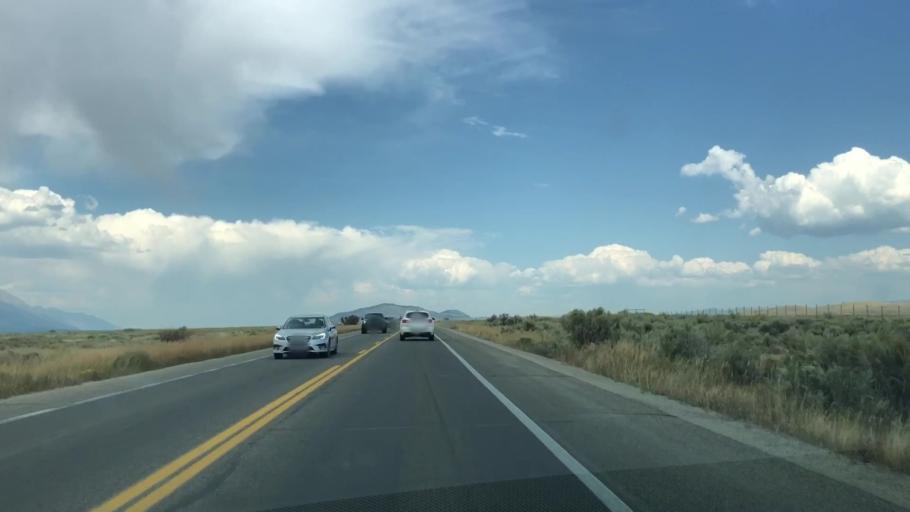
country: US
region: Wyoming
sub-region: Teton County
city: Jackson
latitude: 43.5412
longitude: -110.7357
